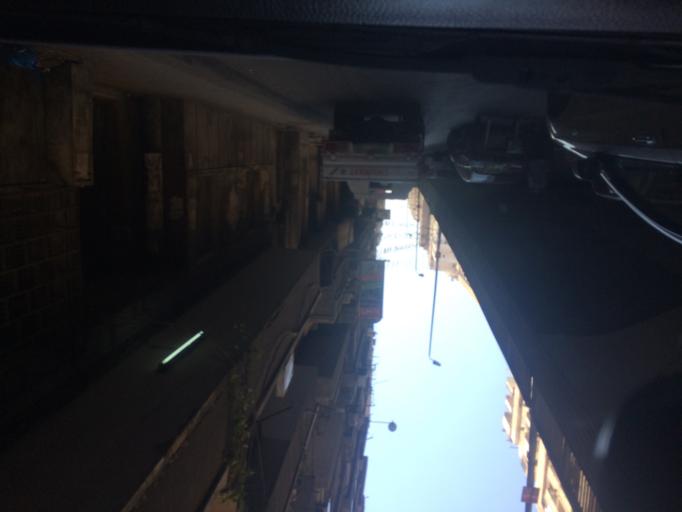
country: EG
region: Alexandria
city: Alexandria
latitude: 31.2666
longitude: 29.9991
